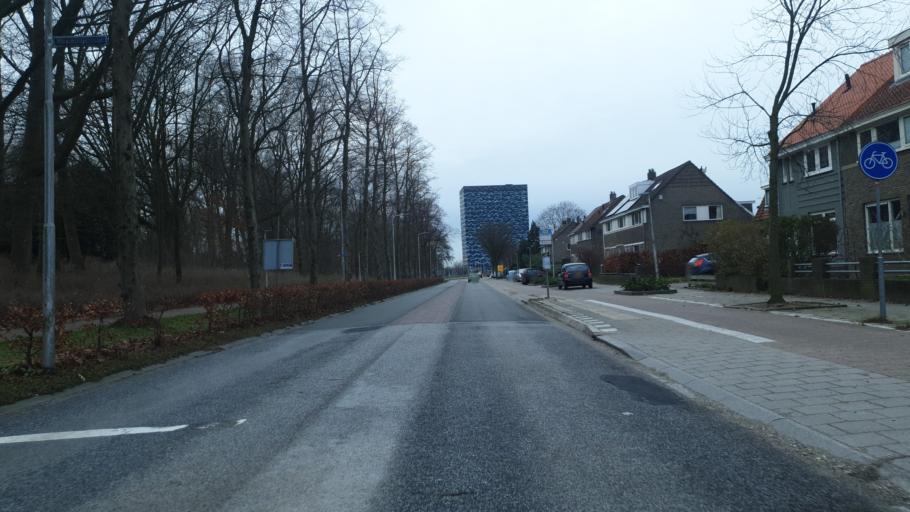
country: NL
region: Gelderland
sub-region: Gemeente Nijmegen
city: Nijmegen
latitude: 51.8286
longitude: 5.8319
